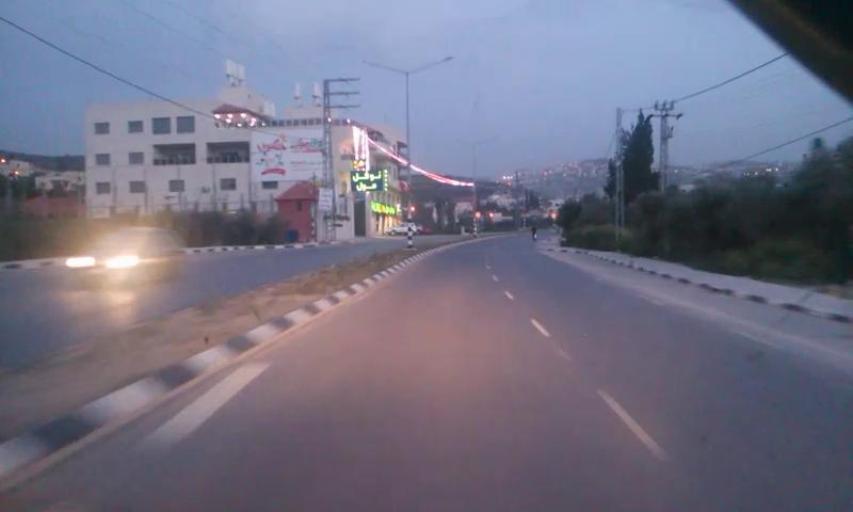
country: PS
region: West Bank
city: Dayr Sharaf
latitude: 32.2505
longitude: 35.1891
